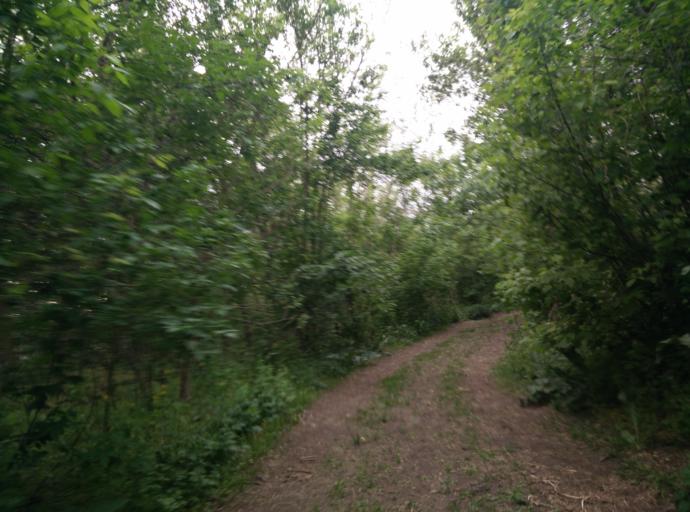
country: HU
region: Pest
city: Fot
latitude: 47.6060
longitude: 19.1805
